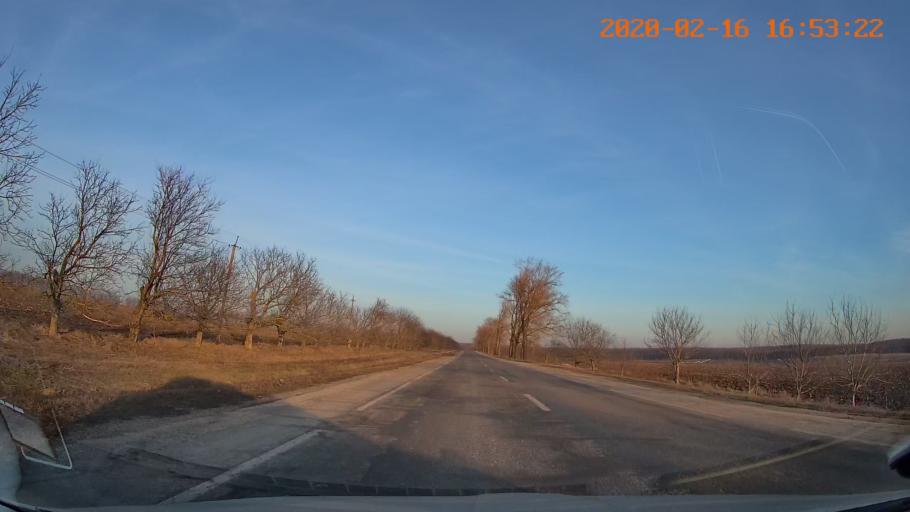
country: MD
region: Briceni
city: Briceni
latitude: 48.3165
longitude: 26.9818
